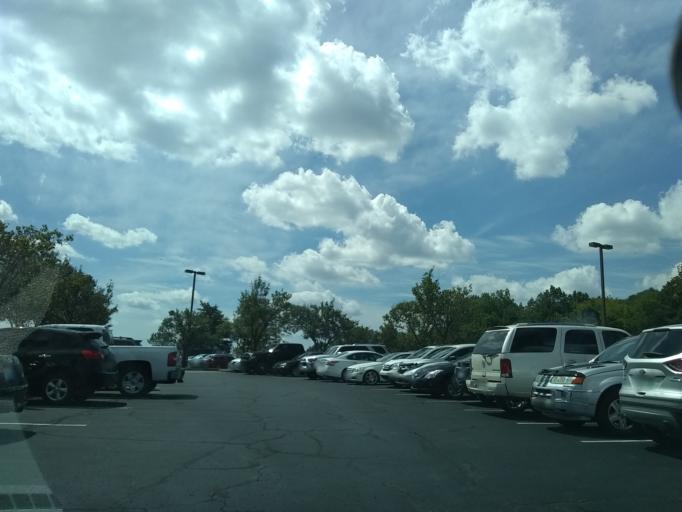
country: US
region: Tennessee
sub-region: Davidson County
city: Nashville
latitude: 36.1386
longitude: -86.6984
